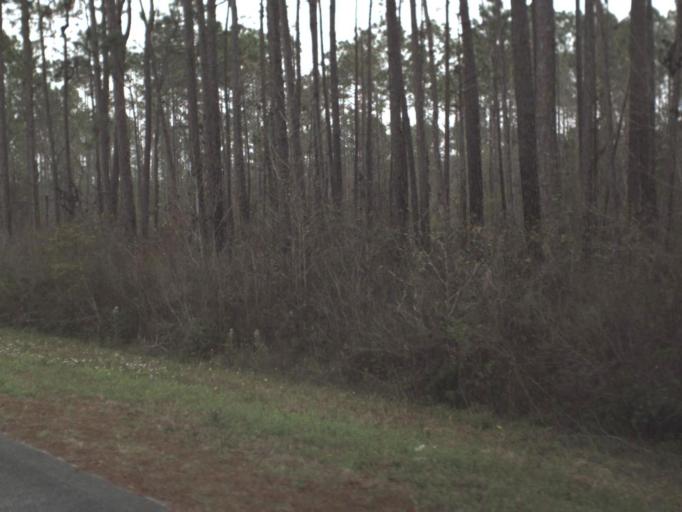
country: US
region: Florida
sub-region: Franklin County
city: Eastpoint
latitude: 29.8278
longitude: -84.8964
